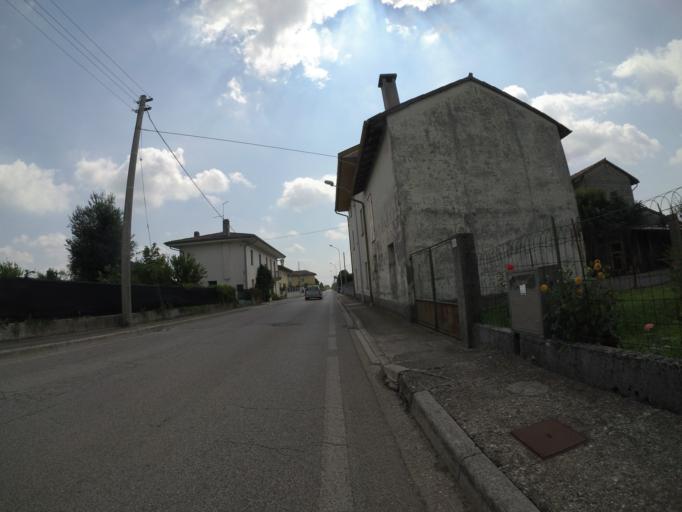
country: IT
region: Friuli Venezia Giulia
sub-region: Provincia di Udine
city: Basiliano
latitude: 46.0101
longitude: 13.0708
